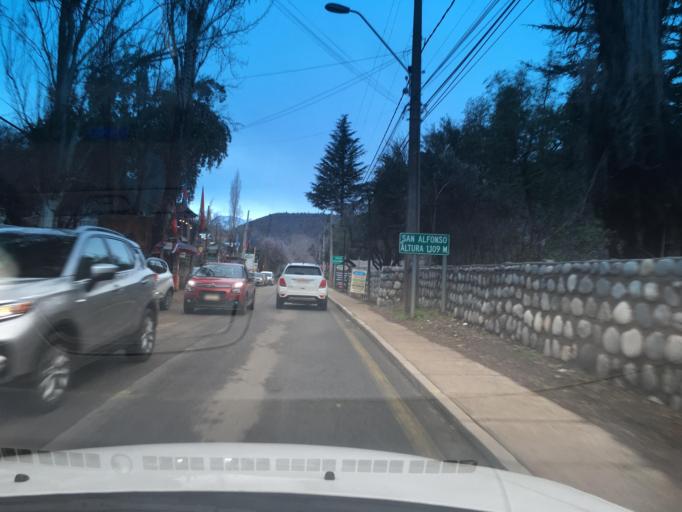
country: CL
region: Santiago Metropolitan
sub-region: Provincia de Cordillera
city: Puente Alto
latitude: -33.7266
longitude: -70.3198
